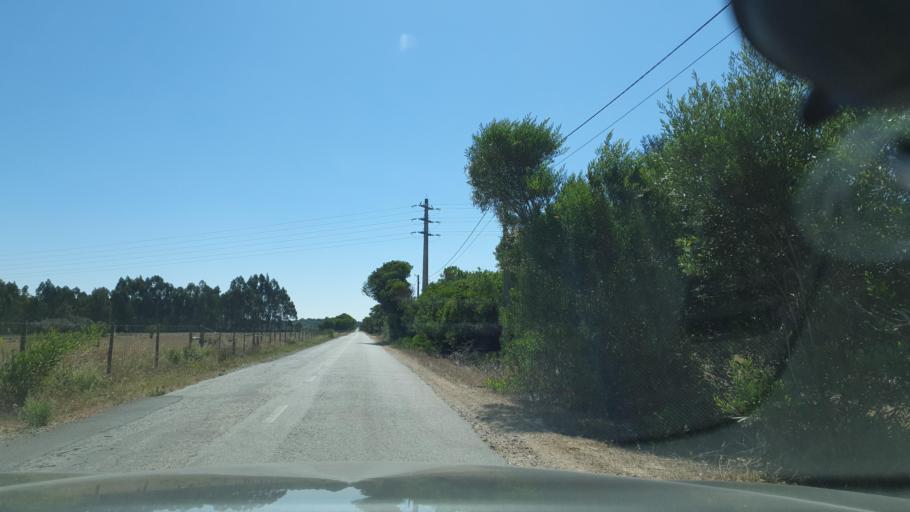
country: PT
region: Beja
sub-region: Odemira
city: Sao Teotonio
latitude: 37.5012
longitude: -8.6845
